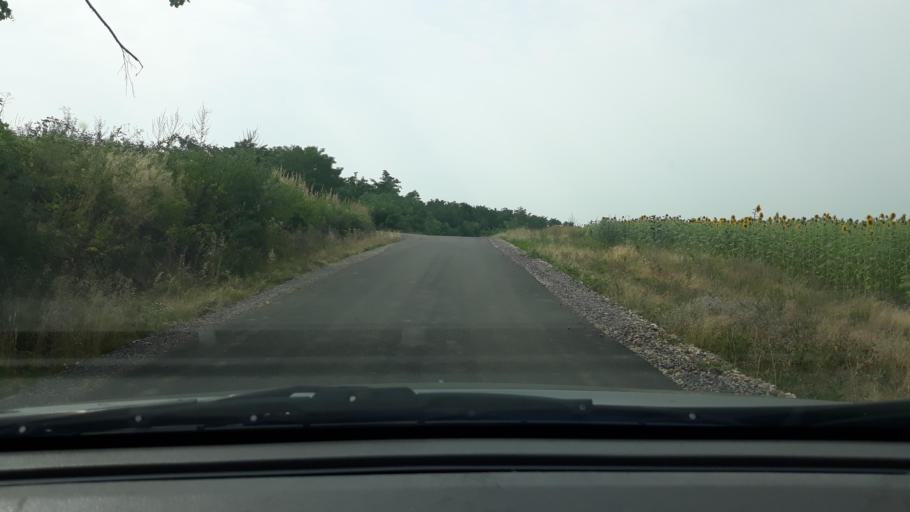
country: RO
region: Bihor
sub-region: Comuna Chislaz
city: Misca
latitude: 47.2613
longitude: 22.2937
